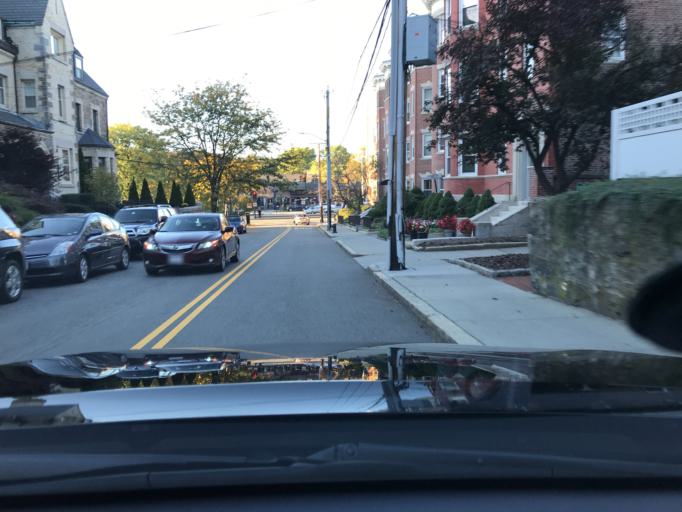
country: US
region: Massachusetts
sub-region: Norfolk County
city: Brookline
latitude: 42.3376
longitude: -71.1385
